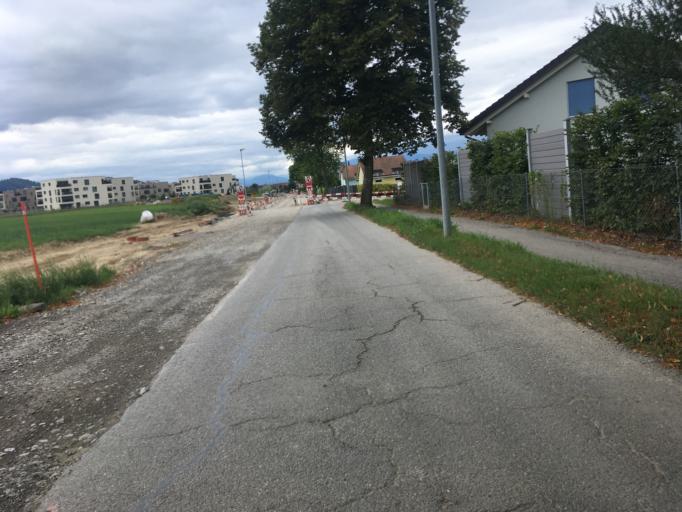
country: CH
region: Fribourg
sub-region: Broye District
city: Estavayer-le-Lac
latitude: 46.8528
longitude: 6.8573
